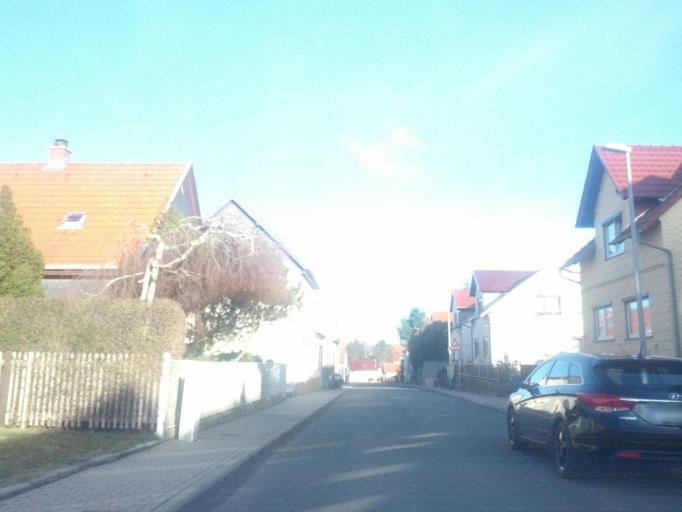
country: DE
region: Thuringia
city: Horselgau
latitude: 50.9191
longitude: 10.5827
